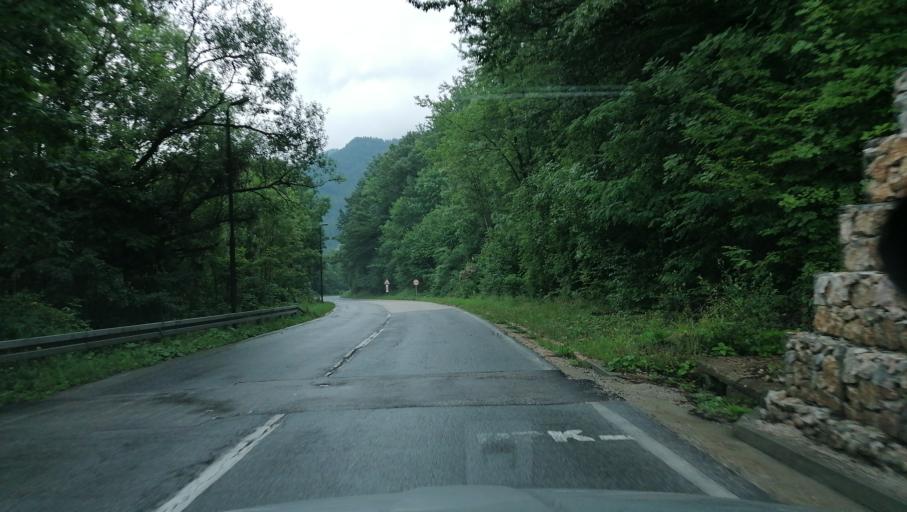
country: RS
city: Durici
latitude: 43.7978
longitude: 19.5087
